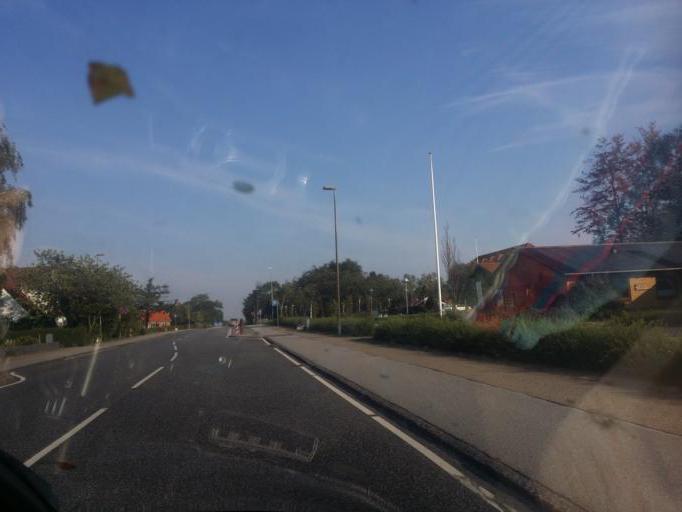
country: DK
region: South Denmark
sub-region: Tonder Kommune
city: Sherrebek
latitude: 55.1529
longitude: 8.7761
